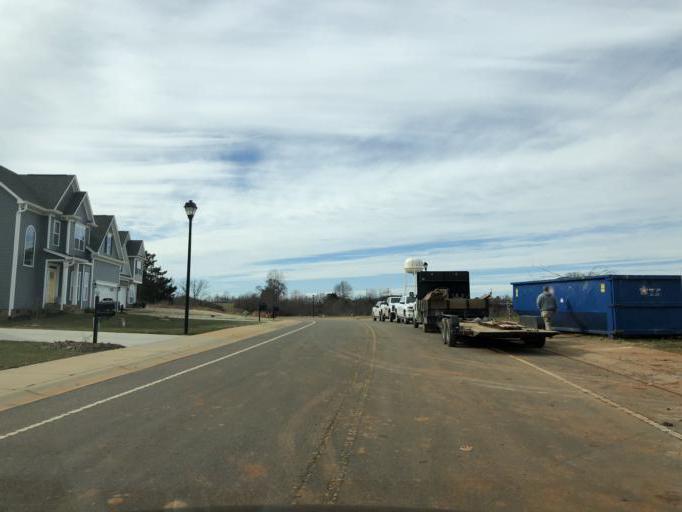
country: US
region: North Carolina
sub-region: Cleveland County
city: Shelby
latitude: 35.2567
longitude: -81.5000
